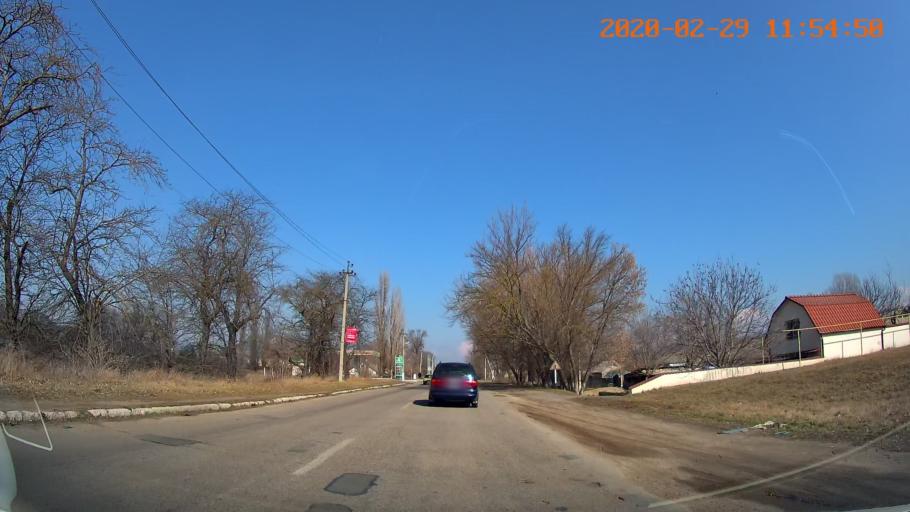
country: MD
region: Telenesti
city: Ribnita
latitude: 47.7866
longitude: 28.9963
